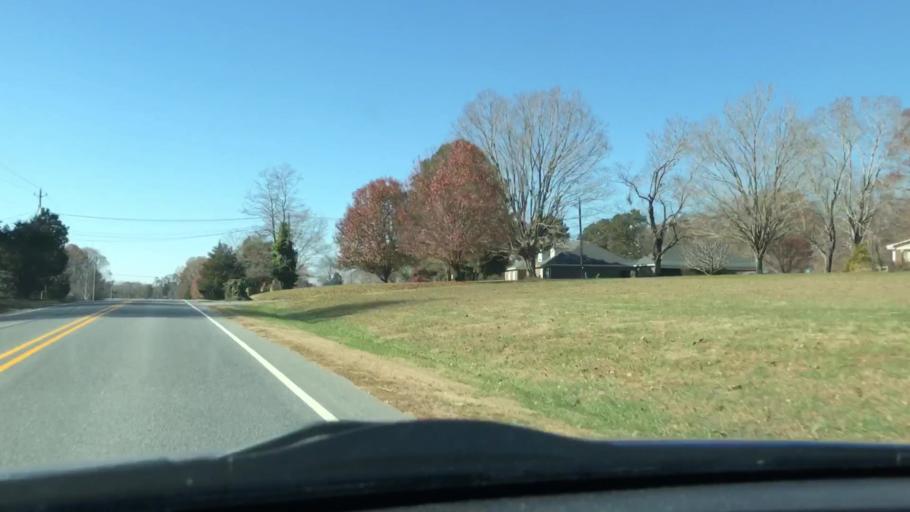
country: US
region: North Carolina
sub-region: Randolph County
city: Asheboro
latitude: 35.6734
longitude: -79.9230
